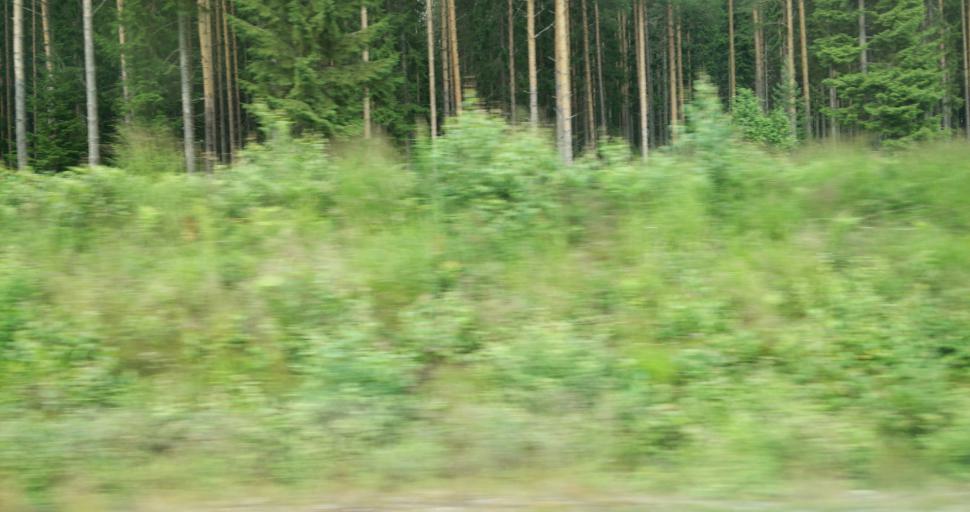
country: SE
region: Vaermland
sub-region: Hagfors Kommun
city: Ekshaerad
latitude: 60.0422
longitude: 13.5314
